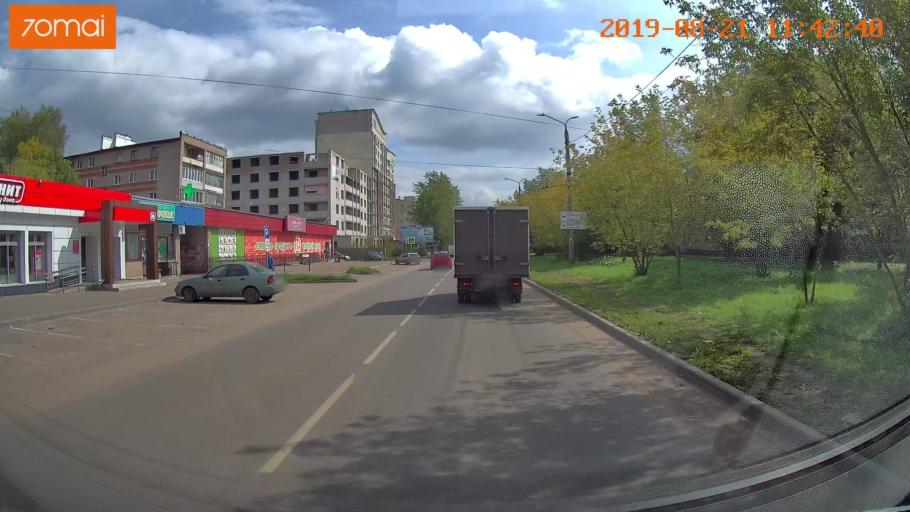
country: RU
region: Ivanovo
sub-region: Gorod Ivanovo
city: Ivanovo
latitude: 57.0017
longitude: 40.9521
